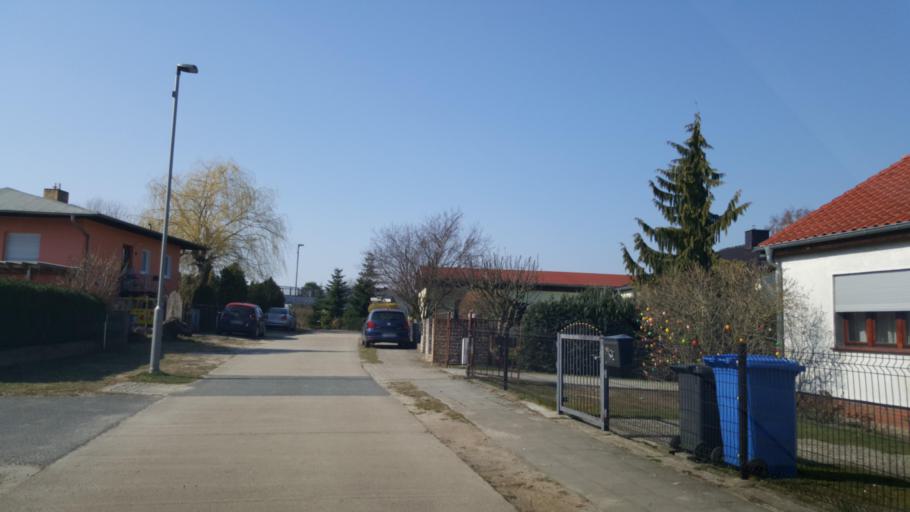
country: DE
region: Berlin
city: Altglienicke
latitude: 52.3993
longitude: 13.5313
